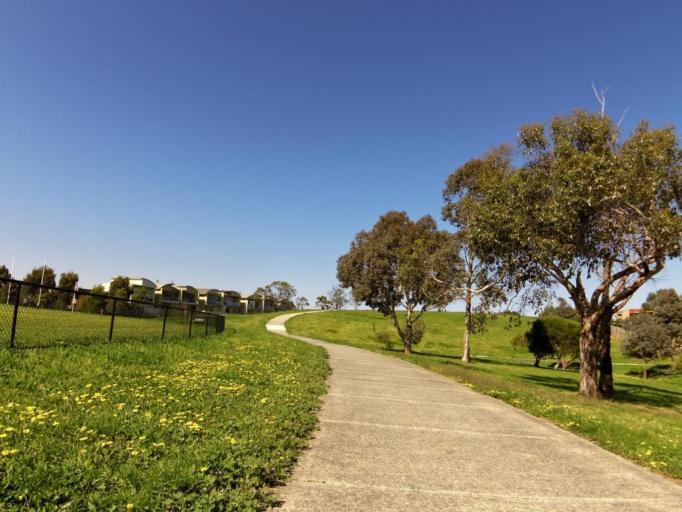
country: AU
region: Victoria
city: Plenty
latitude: -37.6843
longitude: 145.1150
